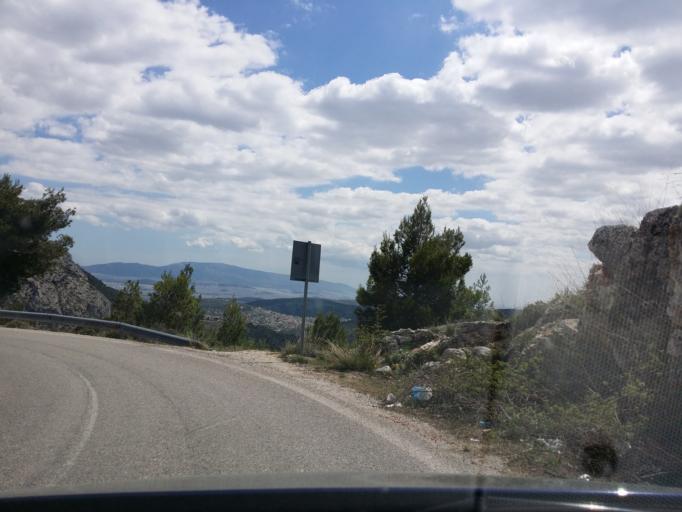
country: GR
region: Attica
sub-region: Nomarchia Dytikis Attikis
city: Fyli
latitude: 38.1333
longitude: 23.6503
